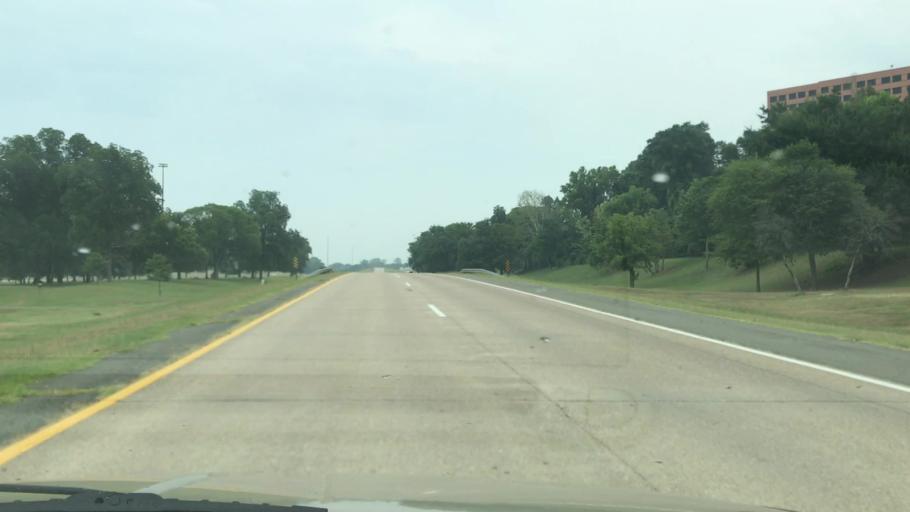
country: US
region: Louisiana
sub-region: Bossier Parish
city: Bossier City
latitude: 32.5057
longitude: -93.7221
